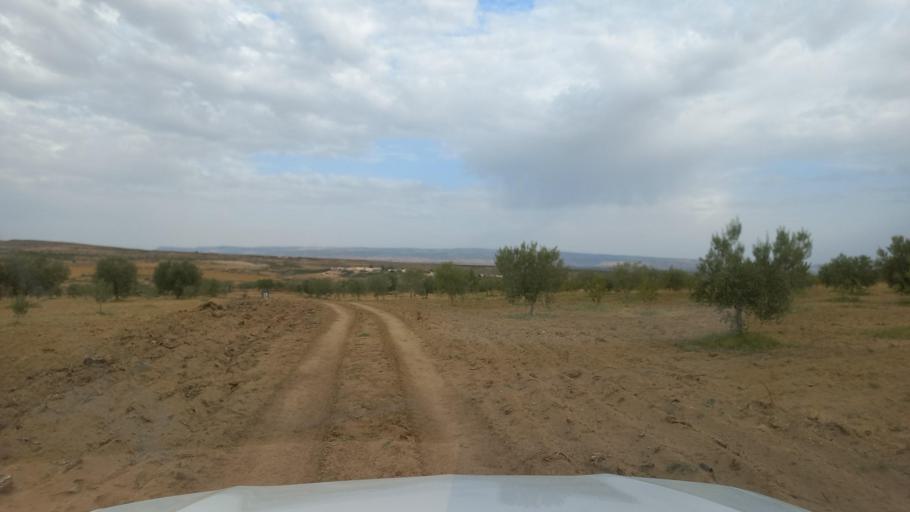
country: TN
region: Al Qasrayn
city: Kasserine
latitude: 35.1941
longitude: 9.0467
